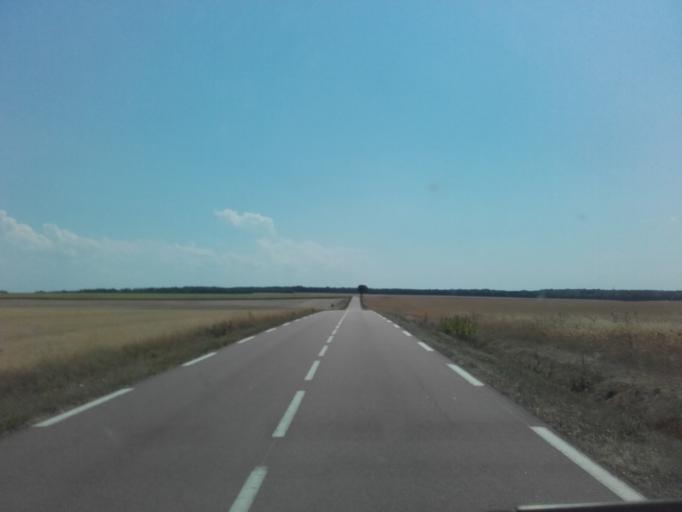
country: FR
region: Bourgogne
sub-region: Departement de l'Yonne
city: Joux-la-Ville
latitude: 47.7225
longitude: 3.8532
